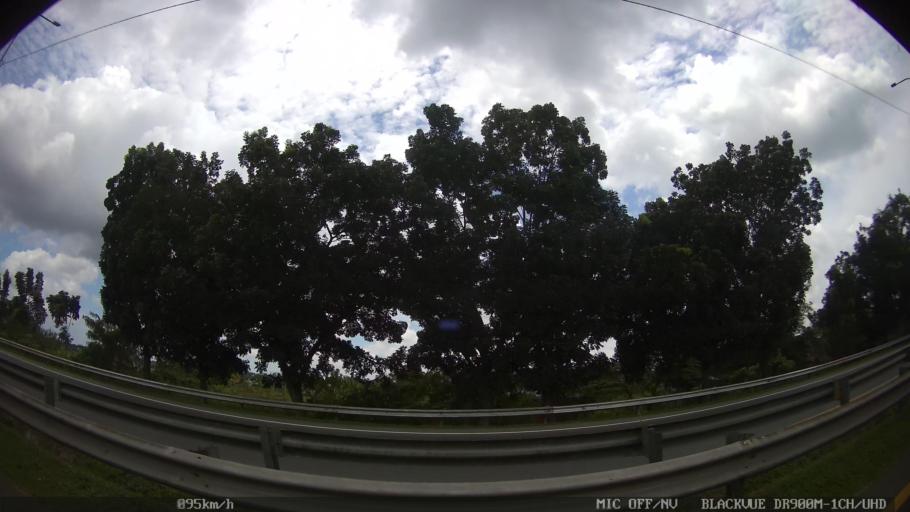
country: ID
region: North Sumatra
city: Medan
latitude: 3.6230
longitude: 98.7198
